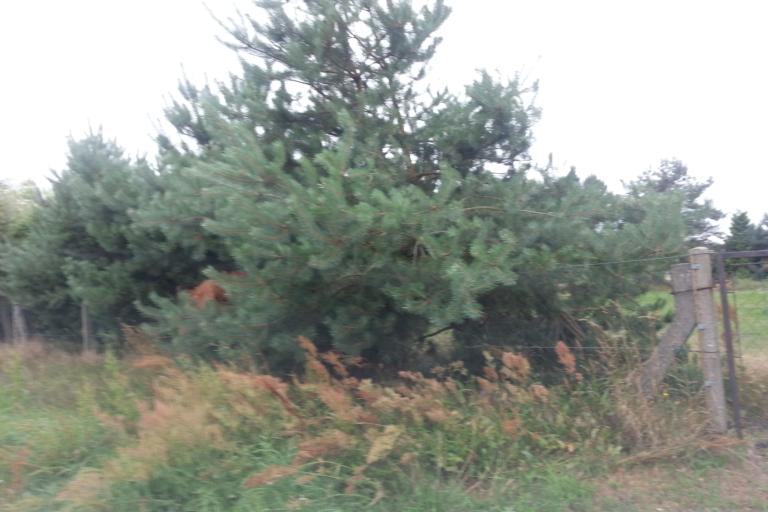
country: DE
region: Mecklenburg-Vorpommern
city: Ferdinandshof
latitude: 53.6838
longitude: 13.9185
